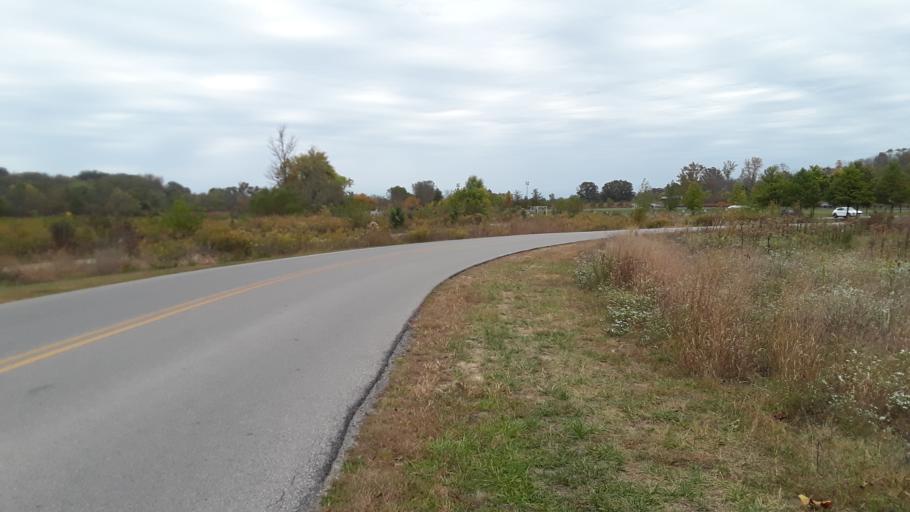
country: US
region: Kentucky
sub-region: Jefferson County
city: Middletown
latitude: 38.2081
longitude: -85.4745
